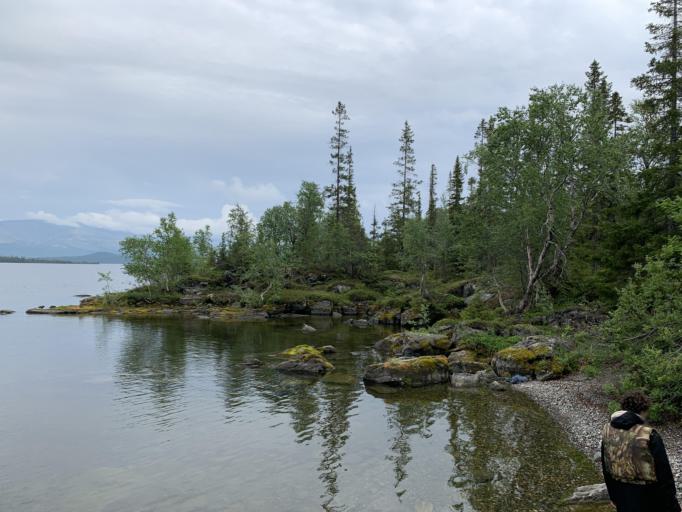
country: RU
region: Murmansk
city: Monchegorsk
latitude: 67.7952
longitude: 33.0527
